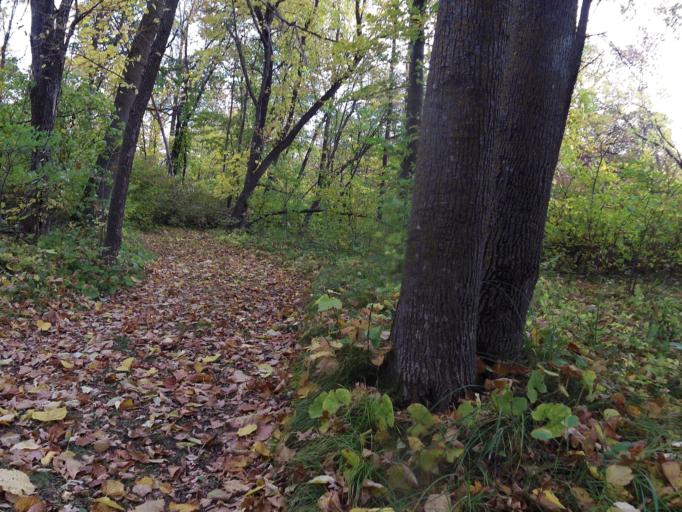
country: US
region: North Dakota
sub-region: Pembina County
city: Cavalier
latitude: 48.7786
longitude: -97.7425
